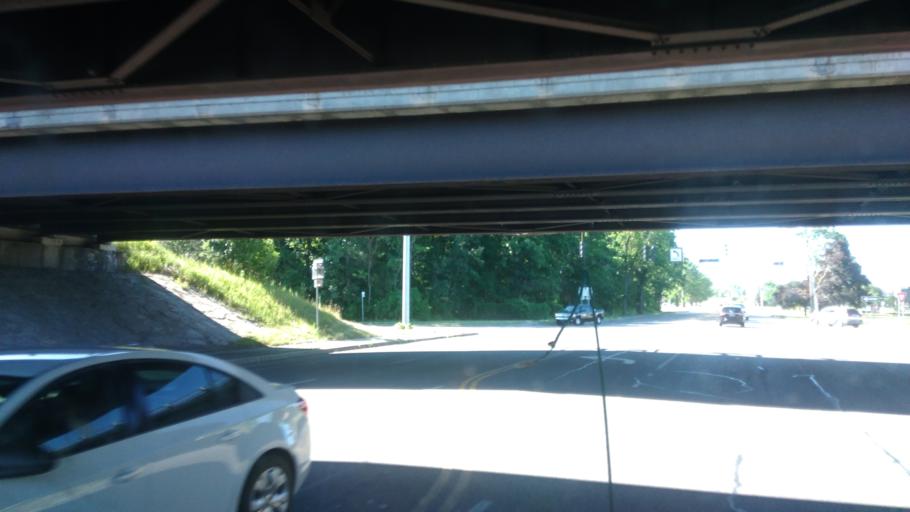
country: US
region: New York
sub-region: Monroe County
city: Webster
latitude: 43.2143
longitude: -77.4613
